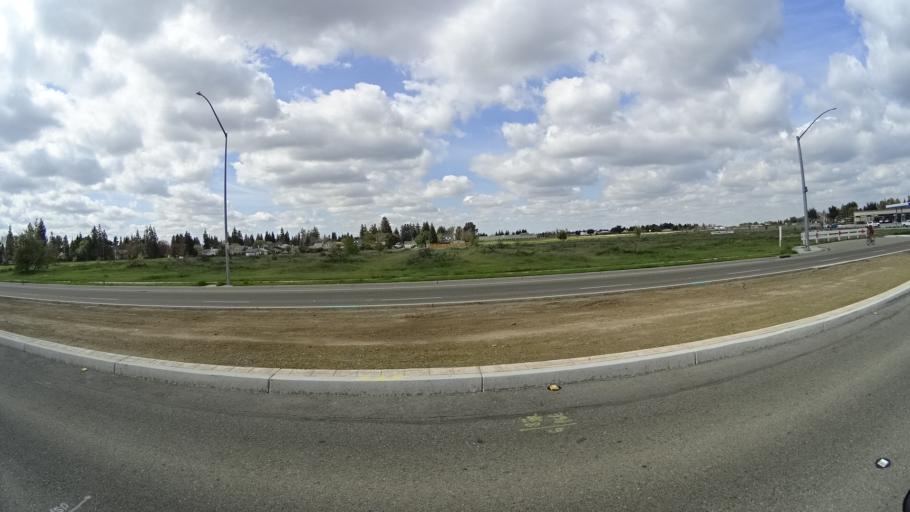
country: US
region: California
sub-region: Fresno County
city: West Park
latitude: 36.8351
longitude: -119.8624
